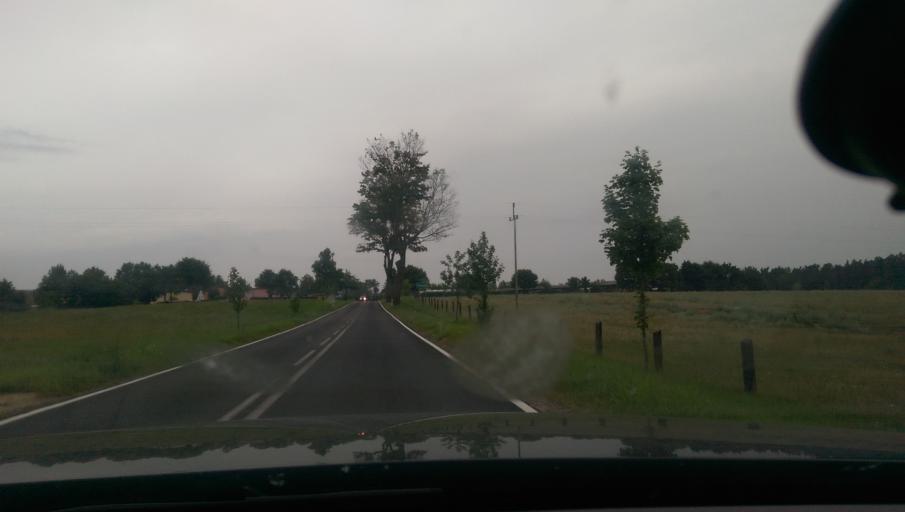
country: PL
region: Warmian-Masurian Voivodeship
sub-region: Powiat piski
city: Orzysz
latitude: 53.8129
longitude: 21.8468
